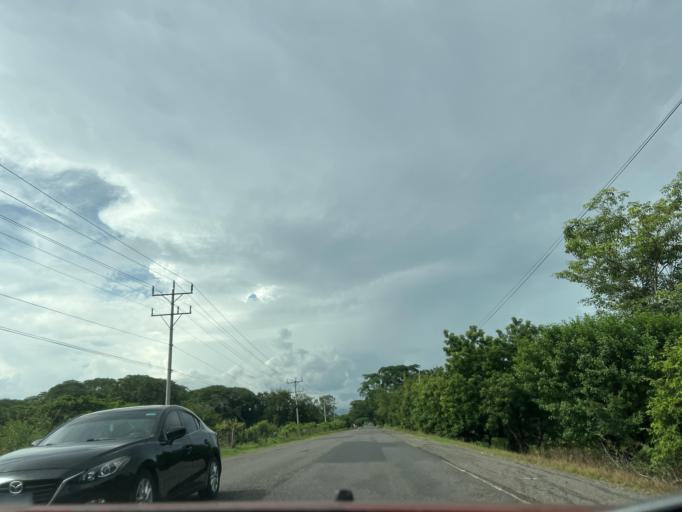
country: SV
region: La Union
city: San Alejo
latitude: 13.3818
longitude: -87.9063
